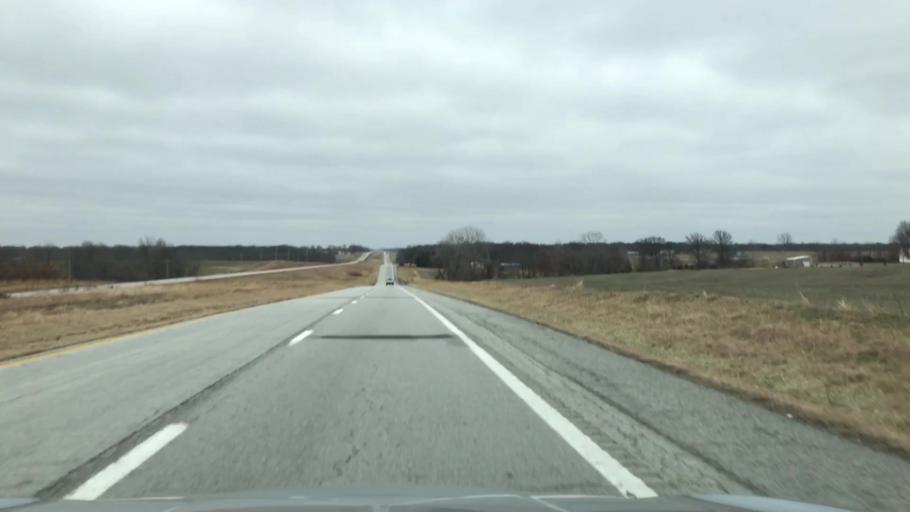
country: US
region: Missouri
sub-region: Linn County
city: Linneus
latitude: 39.7776
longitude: -93.2797
